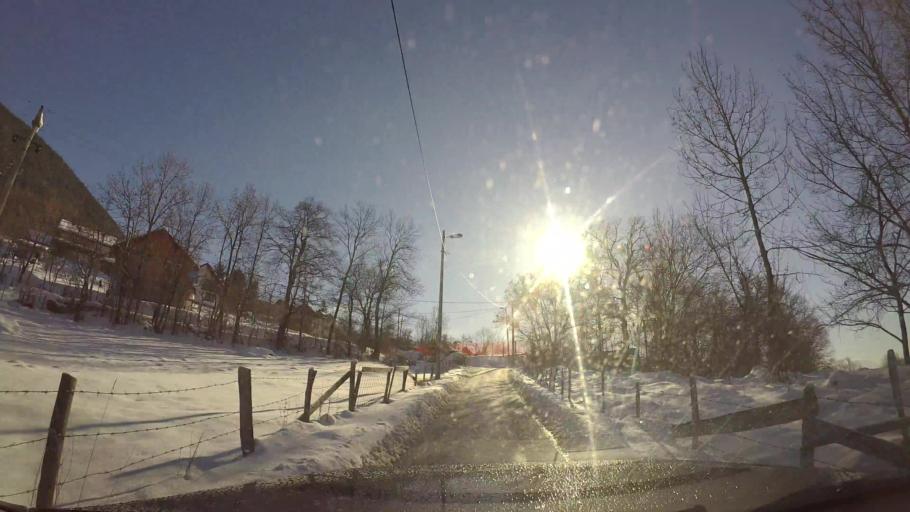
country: BA
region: Federation of Bosnia and Herzegovina
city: Kobilja Glava
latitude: 43.8967
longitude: 18.4158
